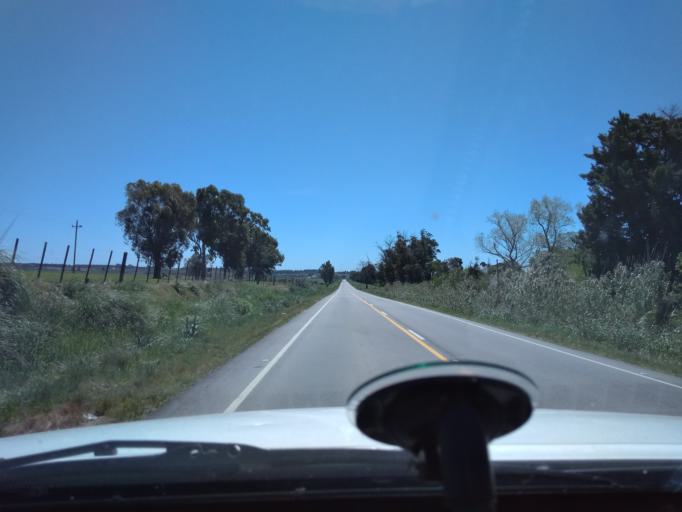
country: UY
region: Canelones
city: Las Piedras
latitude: -34.7078
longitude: -56.2916
